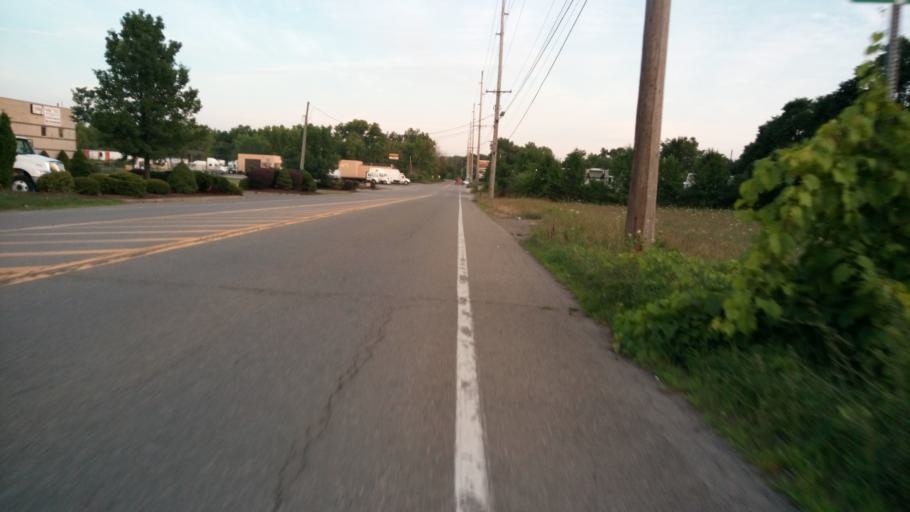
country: US
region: New York
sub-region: Chemung County
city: Elmira Heights
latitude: 42.1213
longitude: -76.8160
